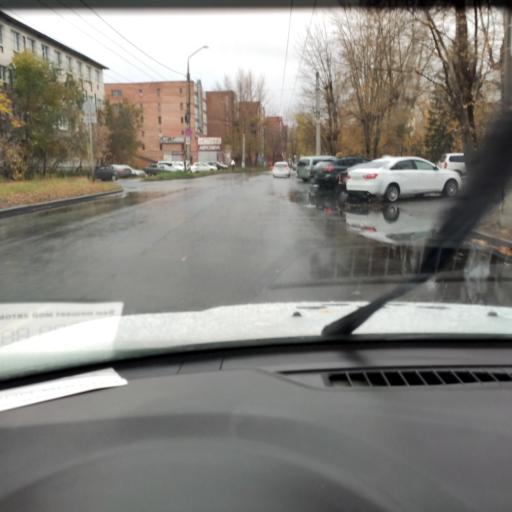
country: RU
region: Samara
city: Tol'yatti
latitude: 53.5149
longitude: 49.4556
